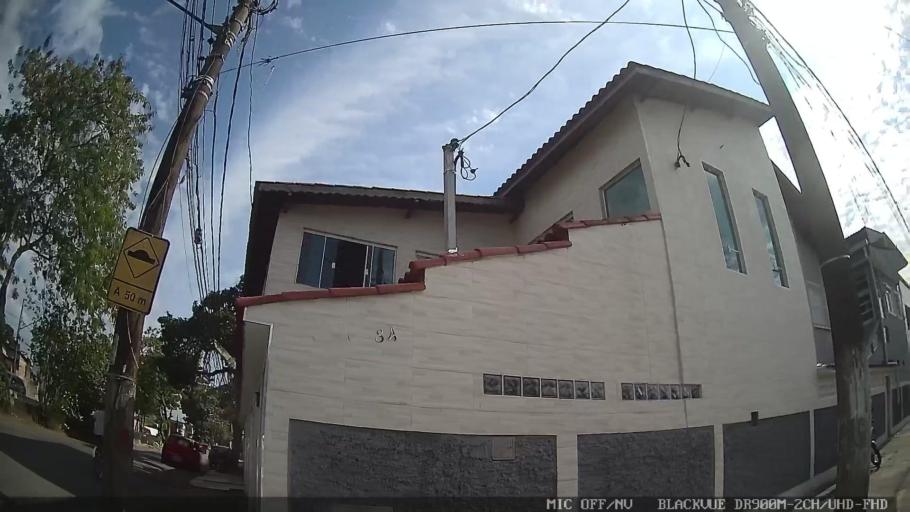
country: BR
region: Sao Paulo
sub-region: Santos
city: Santos
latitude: -23.9452
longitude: -46.2906
